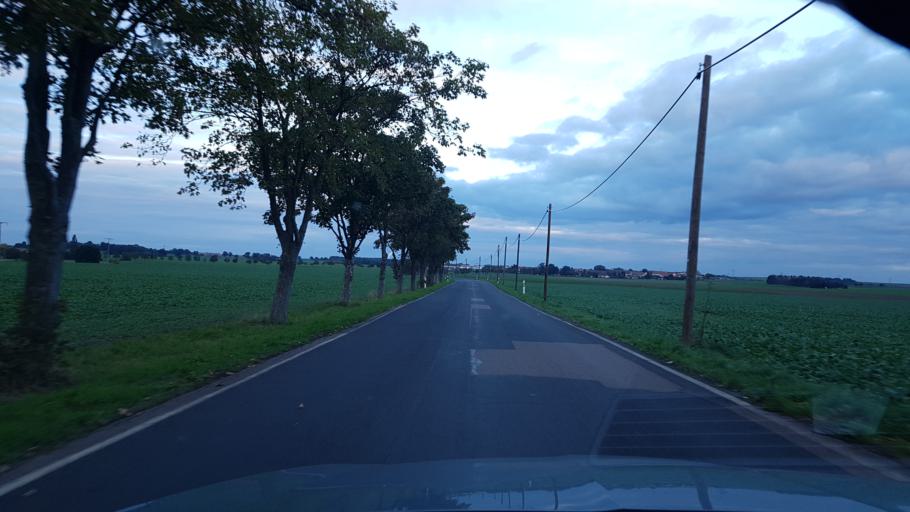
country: DE
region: Saxony
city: Priestewitz
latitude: 51.2430
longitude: 13.5661
